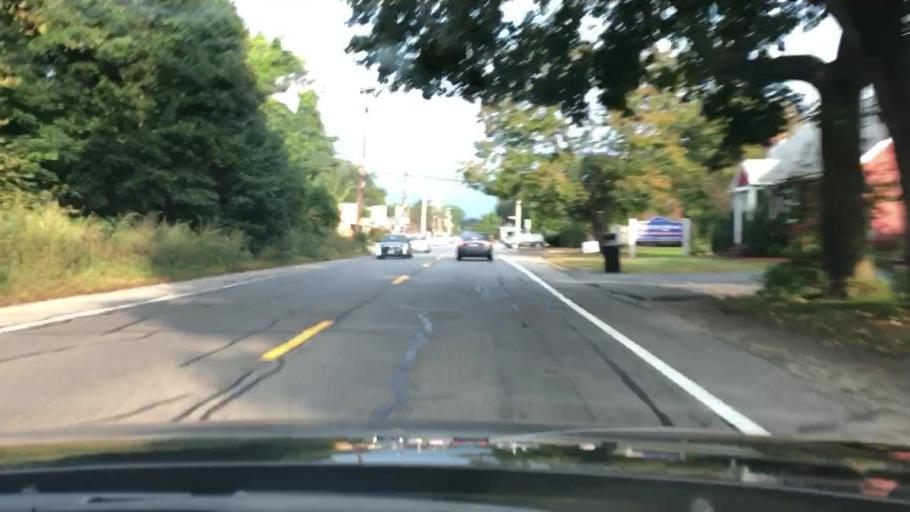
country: US
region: Massachusetts
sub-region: Middlesex County
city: Tyngsboro
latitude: 42.6439
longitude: -71.3904
